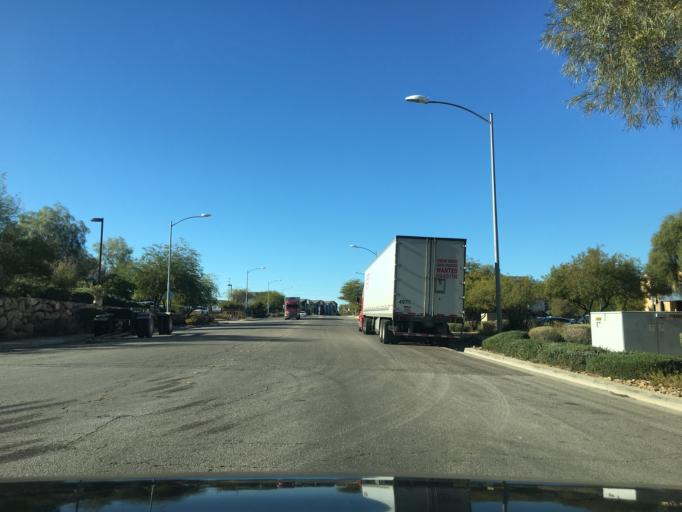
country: US
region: Nevada
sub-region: Clark County
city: Henderson
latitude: 36.0354
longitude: -115.0241
